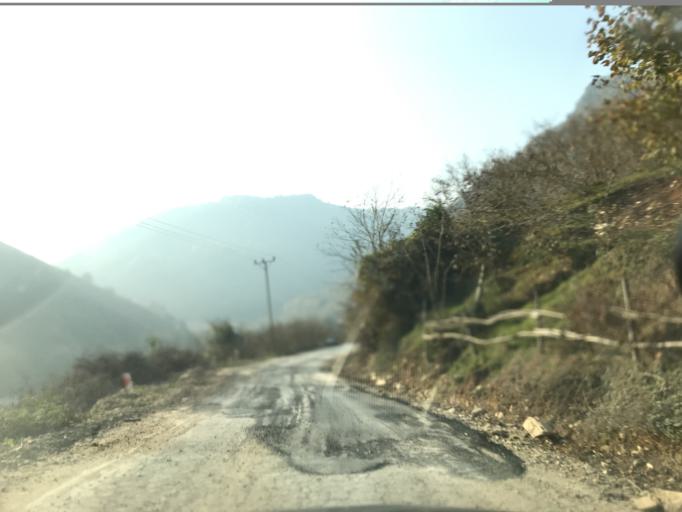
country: TR
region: Duzce
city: Cumayeri
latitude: 40.9357
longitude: 30.9287
